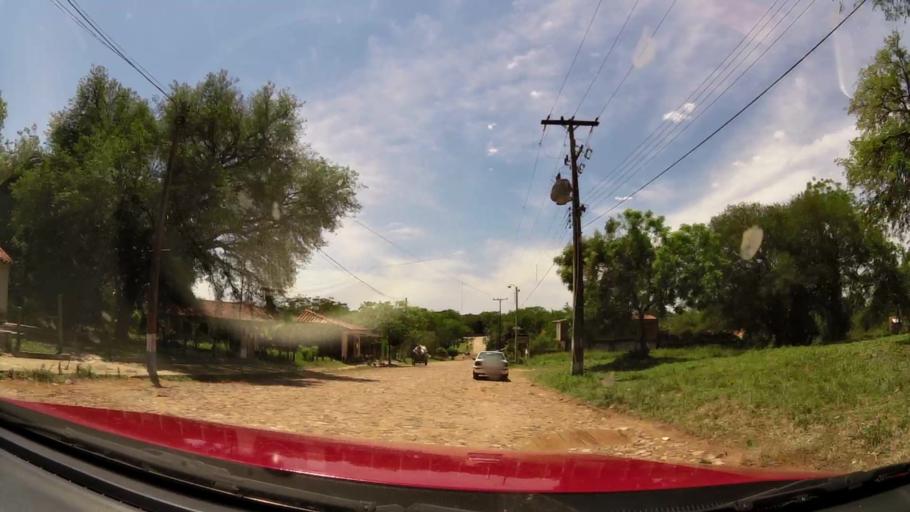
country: PY
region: Central
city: Colonia Mariano Roque Alonso
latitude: -25.1982
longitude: -57.5502
